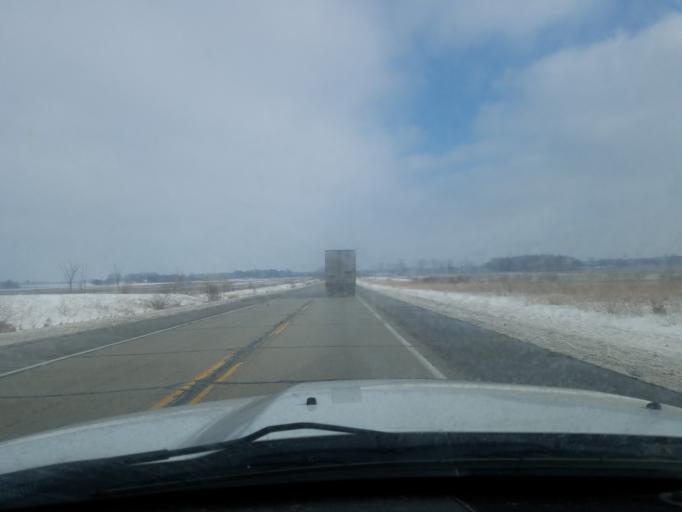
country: US
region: Indiana
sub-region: Marshall County
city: Bremen
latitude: 41.4606
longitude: -86.1900
